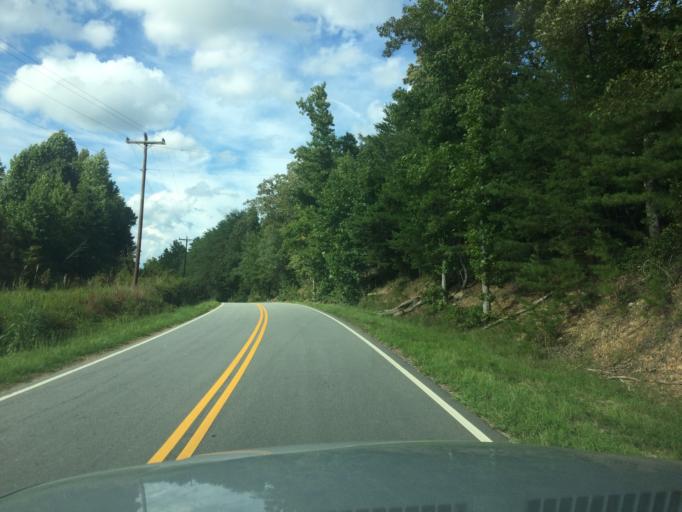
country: US
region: South Carolina
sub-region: Spartanburg County
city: Woodruff
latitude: 34.7442
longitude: -82.1104
